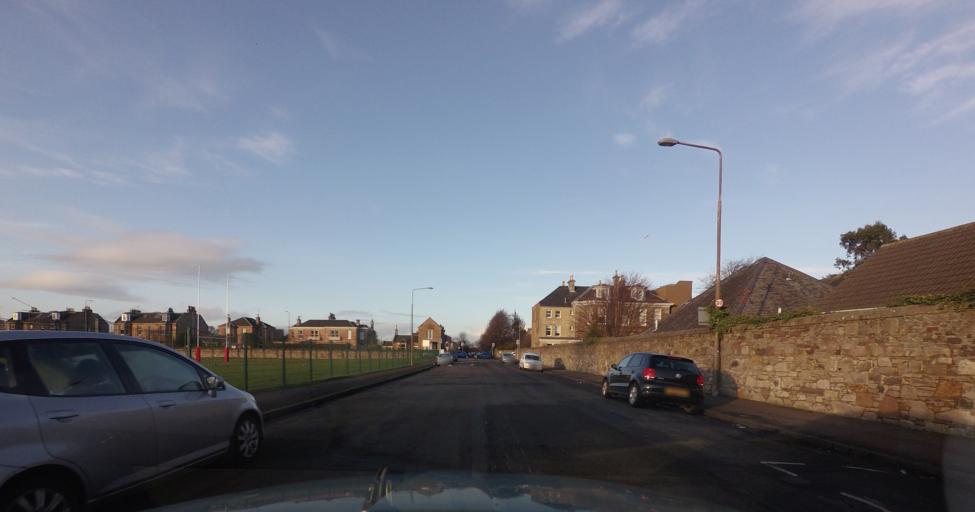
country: GB
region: Scotland
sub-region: Edinburgh
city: Edinburgh
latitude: 55.9698
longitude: -3.2157
